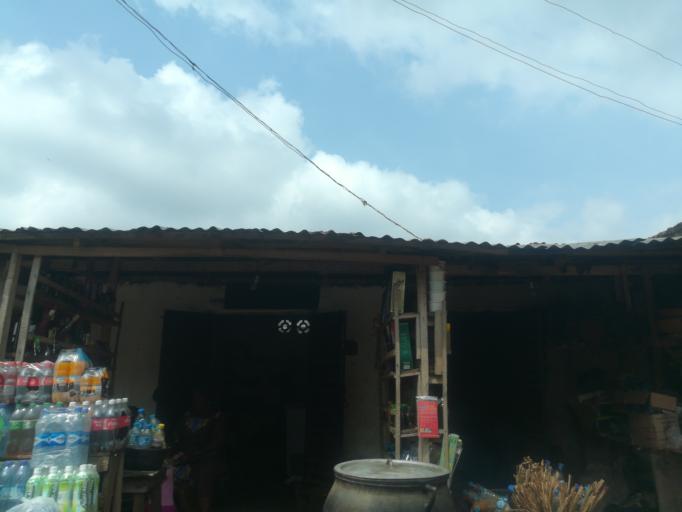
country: NG
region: Oyo
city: Ibadan
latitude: 7.4118
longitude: 3.9506
